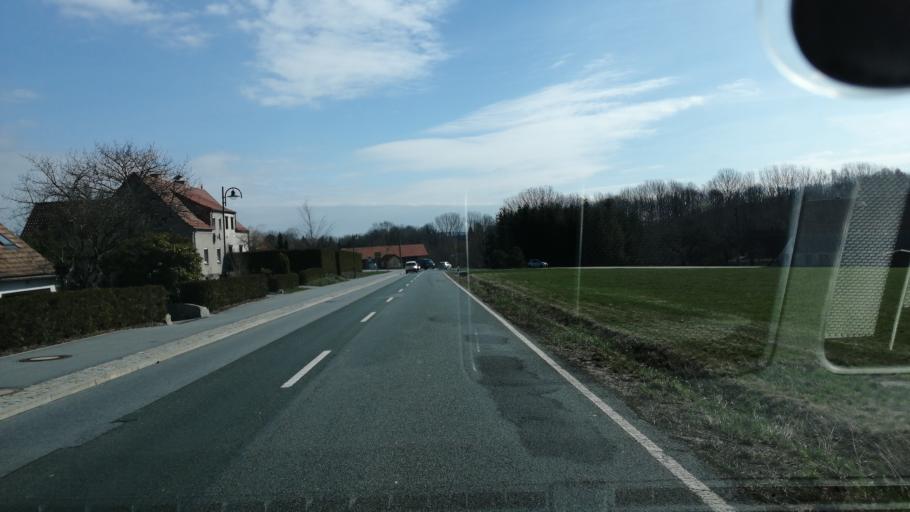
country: DE
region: Saxony
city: Lawalde
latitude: 51.0808
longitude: 14.6039
